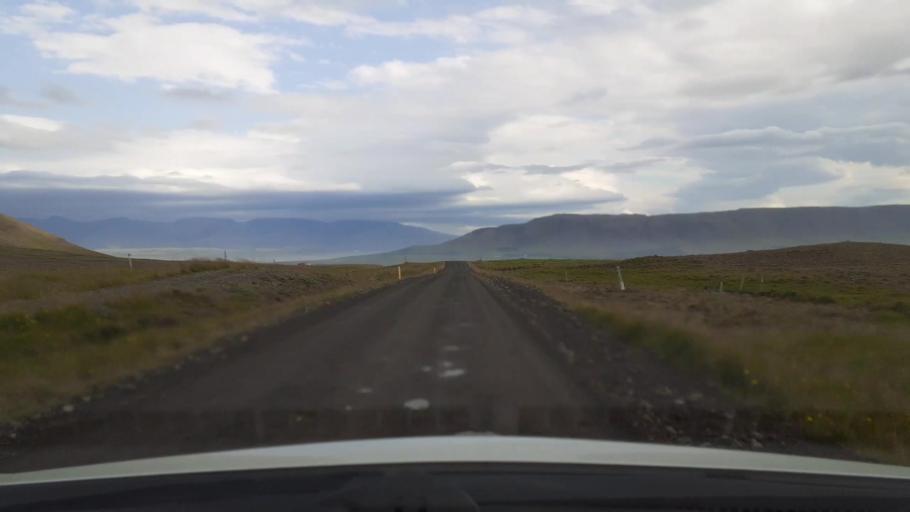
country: IS
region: Capital Region
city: Mosfellsbaer
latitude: 64.3059
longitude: -21.6566
